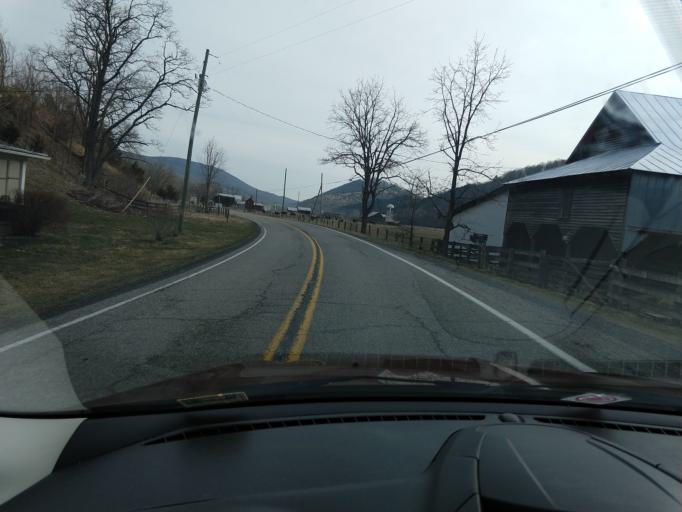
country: US
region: Virginia
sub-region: Highland County
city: Monterey
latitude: 38.4872
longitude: -79.5035
